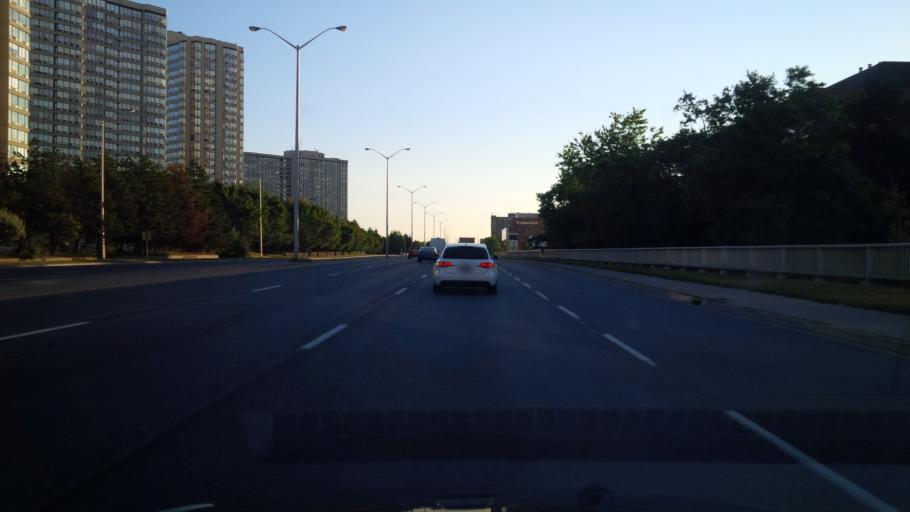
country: CA
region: Ontario
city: Brampton
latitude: 43.7155
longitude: -79.7272
